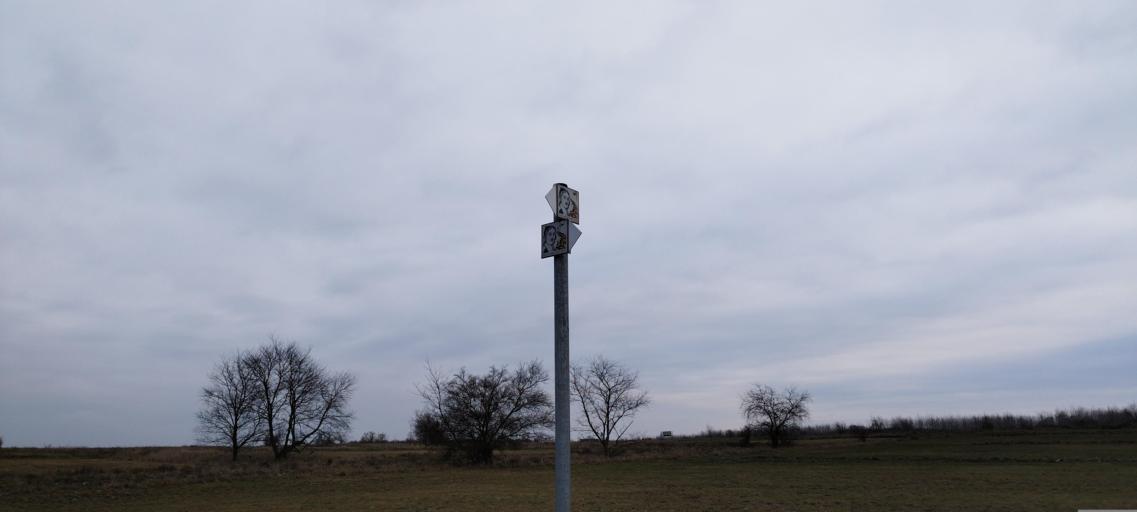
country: DE
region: Brandenburg
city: Mittenwalde
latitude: 52.3069
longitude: 13.5478
